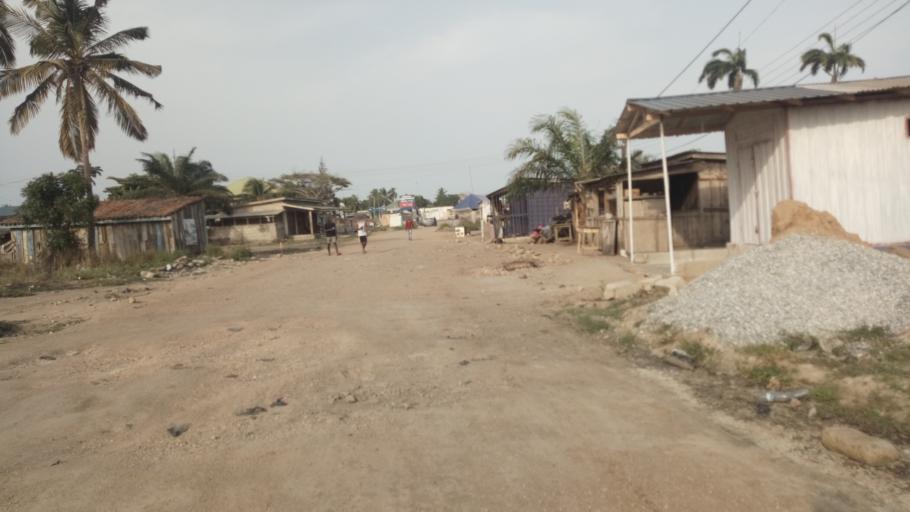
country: GH
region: Central
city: Winneba
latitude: 5.3517
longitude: -0.6321
